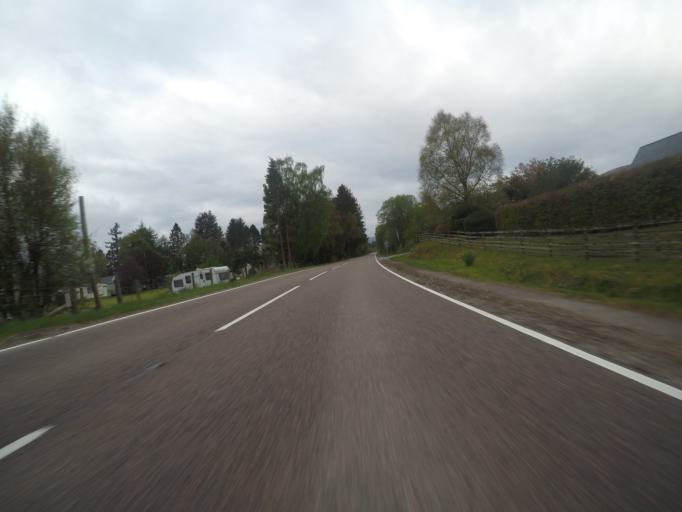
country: GB
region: Scotland
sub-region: Highland
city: Spean Bridge
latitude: 56.8895
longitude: -4.8605
